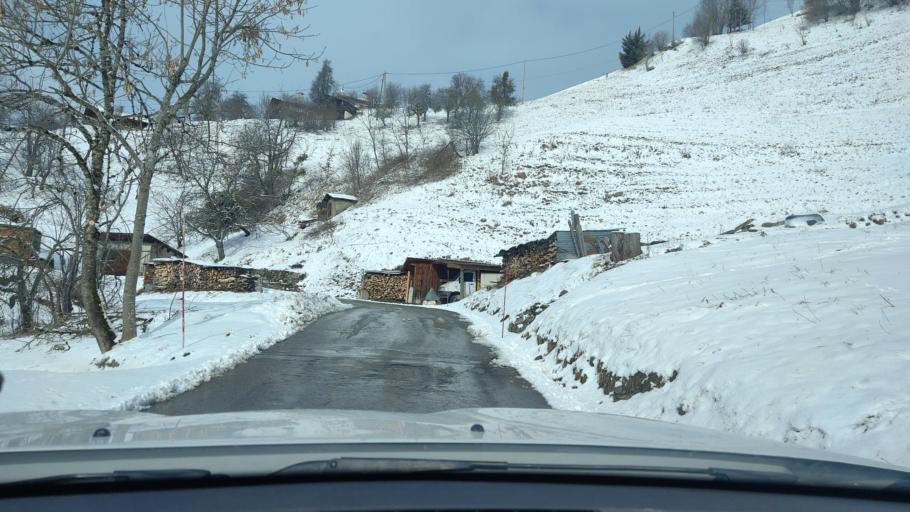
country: FR
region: Rhone-Alpes
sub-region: Departement de la Savoie
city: Beaufort
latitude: 45.7304
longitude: 6.5803
